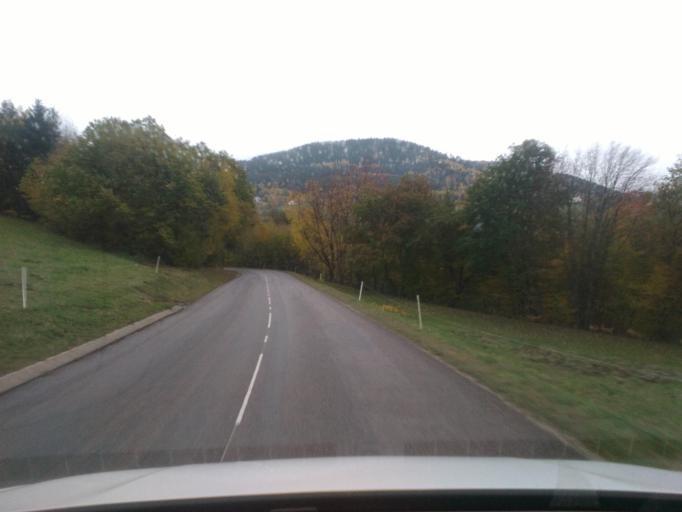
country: FR
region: Lorraine
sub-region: Departement des Vosges
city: Plainfaing
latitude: 48.1876
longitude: 7.0158
